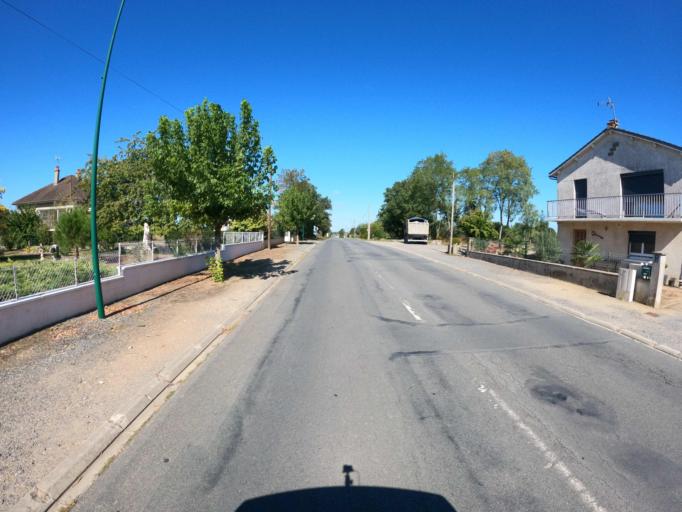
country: FR
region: Poitou-Charentes
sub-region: Departement de la Vienne
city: Lathus-Saint-Remy
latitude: 46.3388
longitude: 0.9550
